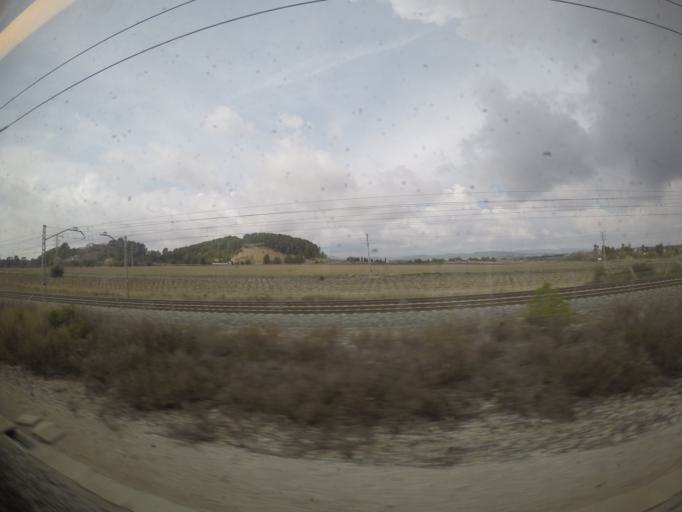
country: ES
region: Catalonia
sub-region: Provincia de Barcelona
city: Castellet
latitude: 41.2784
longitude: 1.6056
